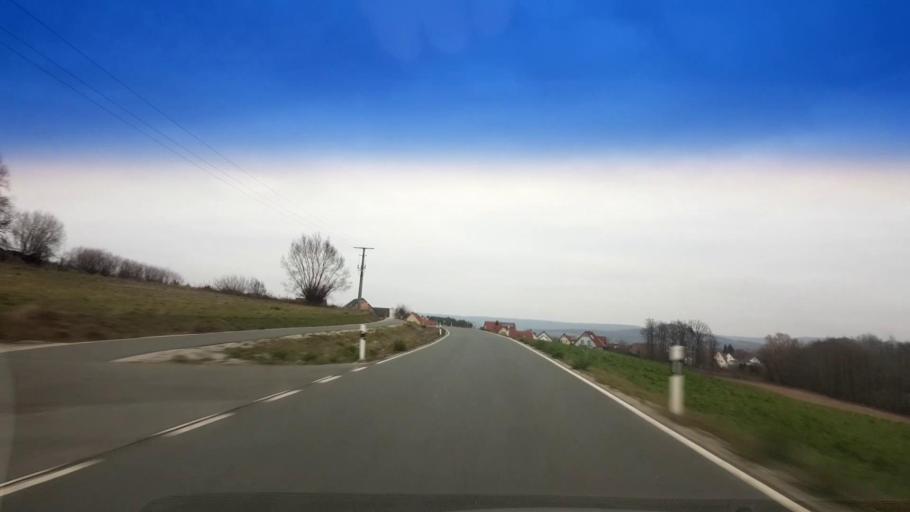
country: DE
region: Bavaria
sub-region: Upper Franconia
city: Hallerndorf
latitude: 49.7699
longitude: 10.9964
